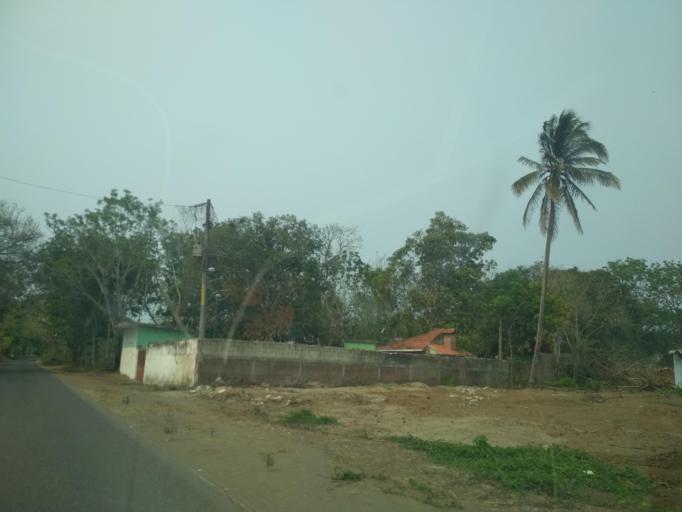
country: MX
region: Veracruz
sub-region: Veracruz
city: Delfino Victoria (Santa Fe)
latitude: 19.2111
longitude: -96.3159
